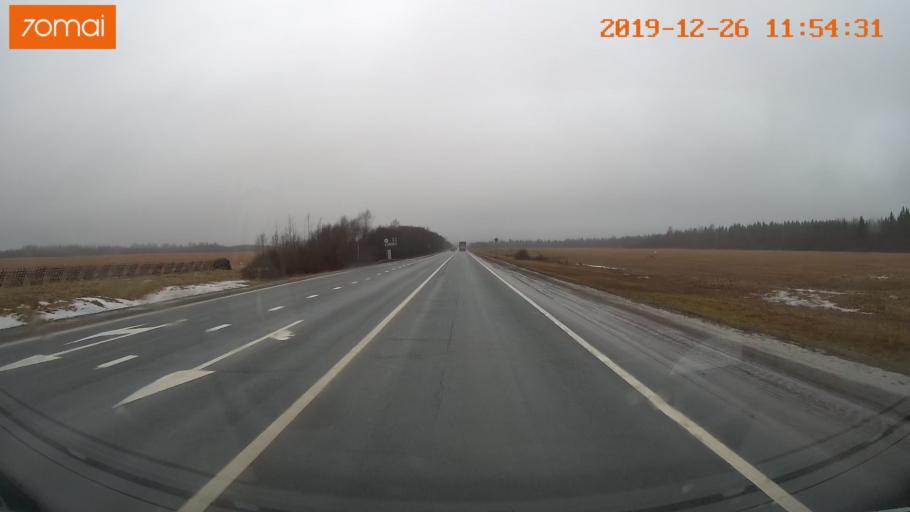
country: RU
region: Vologda
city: Sheksna
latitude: 59.2766
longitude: 38.3033
